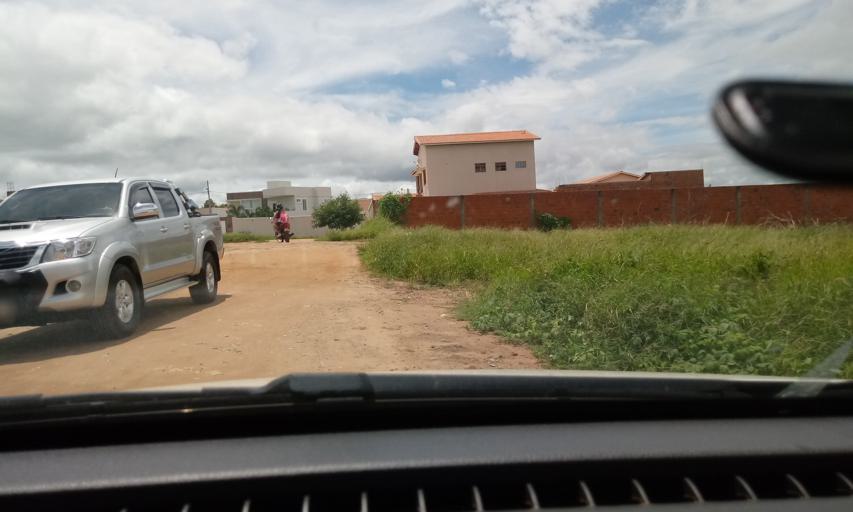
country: BR
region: Bahia
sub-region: Guanambi
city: Guanambi
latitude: -14.2308
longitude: -42.7759
